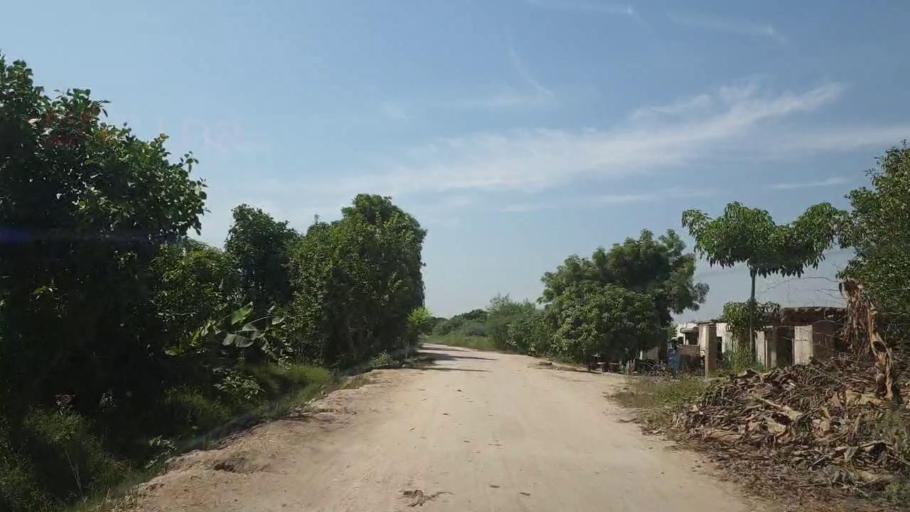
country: PK
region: Sindh
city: Tando Allahyar
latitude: 25.3991
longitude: 68.6368
